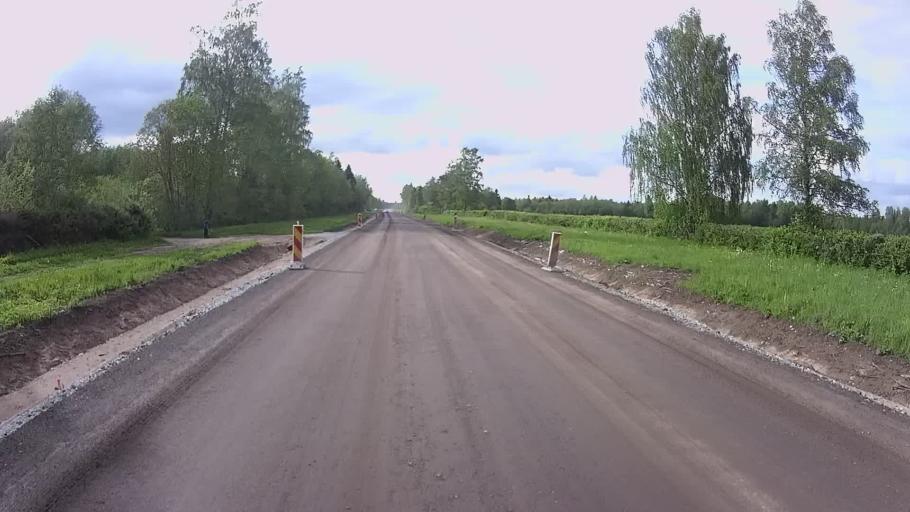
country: EE
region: Jogevamaa
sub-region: Mustvee linn
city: Mustvee
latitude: 59.0236
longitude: 26.6984
